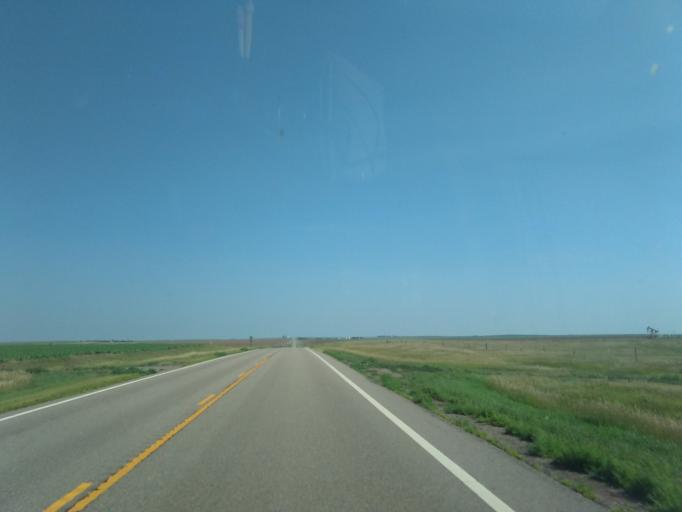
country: US
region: Kansas
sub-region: Cheyenne County
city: Saint Francis
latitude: 39.5754
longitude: -101.7135
